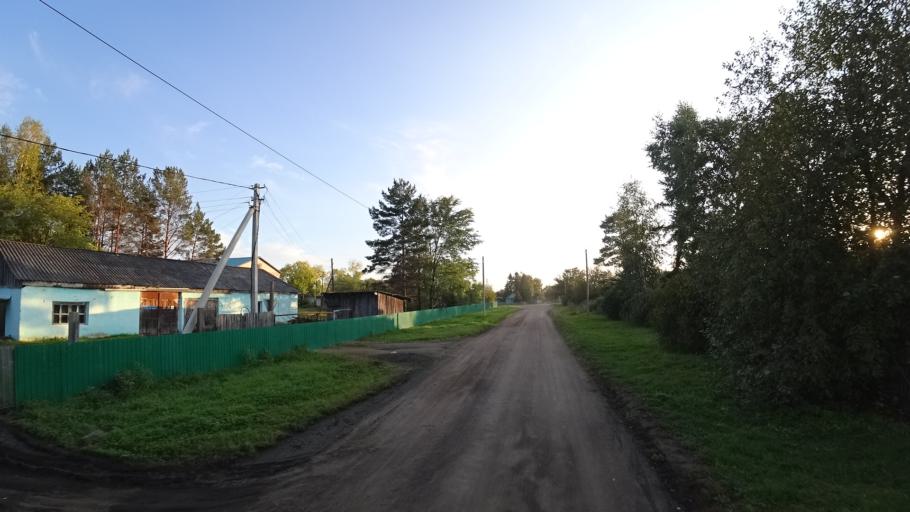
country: RU
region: Amur
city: Arkhara
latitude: 49.3616
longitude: 130.1156
